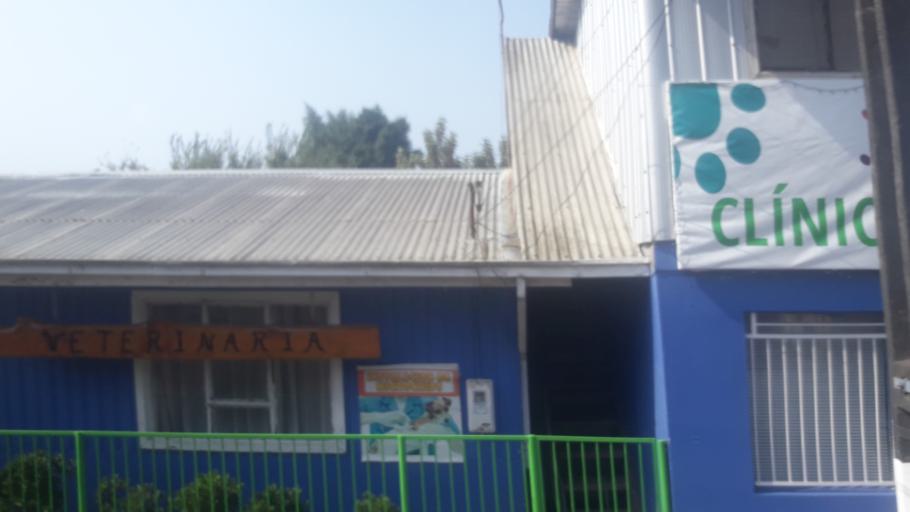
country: CL
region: Biobio
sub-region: Provincia de Concepcion
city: Lota
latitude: -37.1738
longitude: -72.9405
